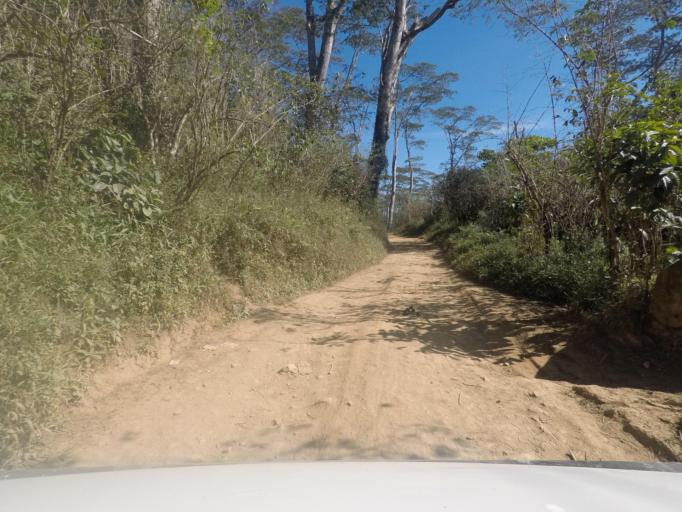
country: TL
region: Ermera
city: Gleno
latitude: -8.7381
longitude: 125.3454
